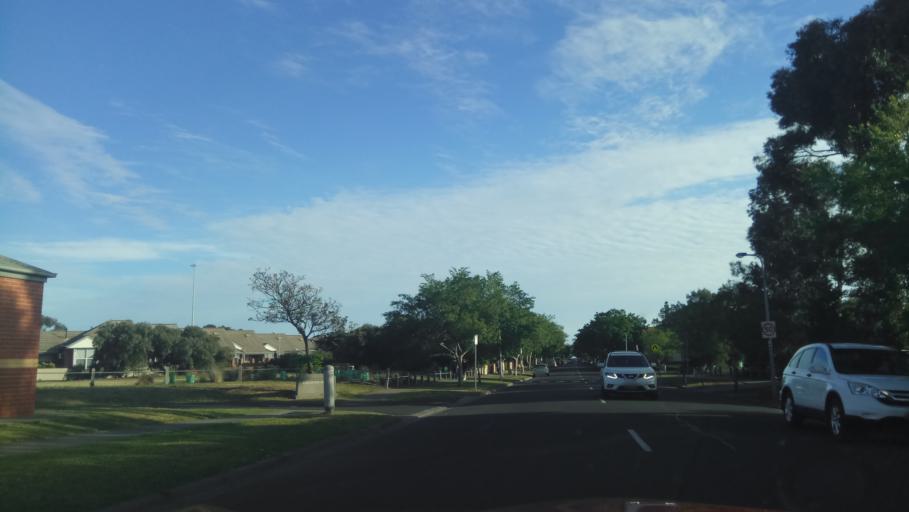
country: AU
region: Victoria
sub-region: Hobsons Bay
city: Williamstown North
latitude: -37.8583
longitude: 144.8829
